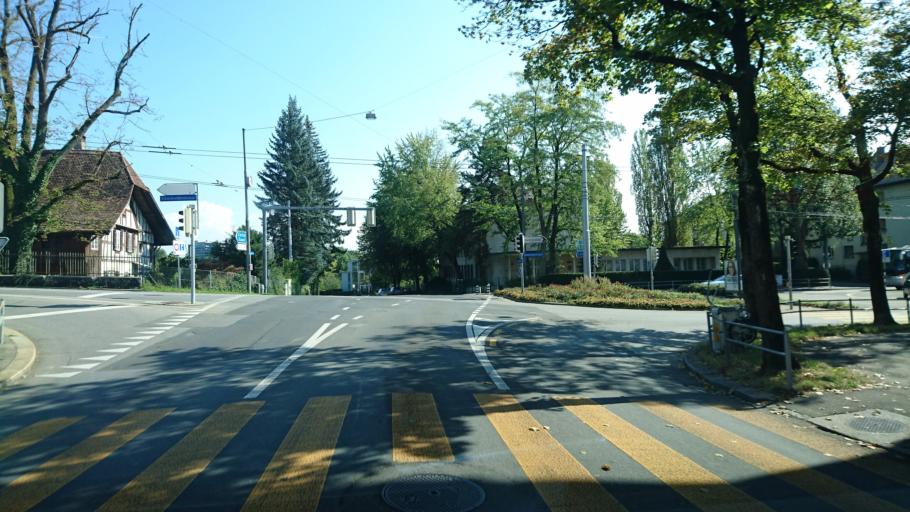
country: CH
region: Bern
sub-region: Bern-Mittelland District
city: Bern
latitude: 46.9477
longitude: 7.4660
